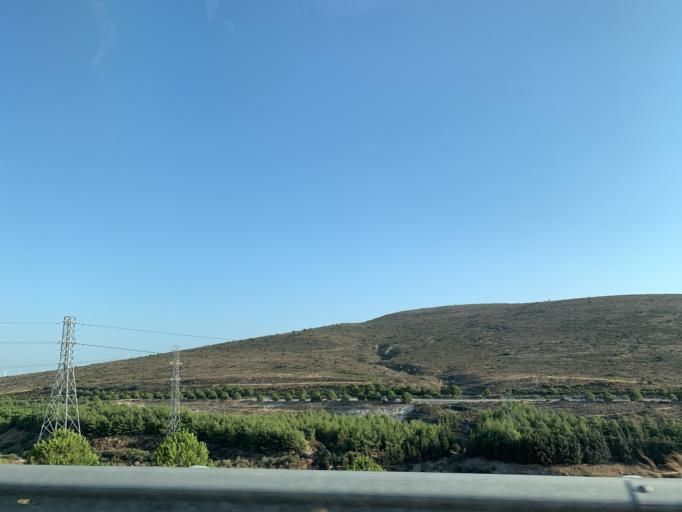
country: TR
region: Izmir
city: Alacati
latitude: 38.2761
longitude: 26.4111
